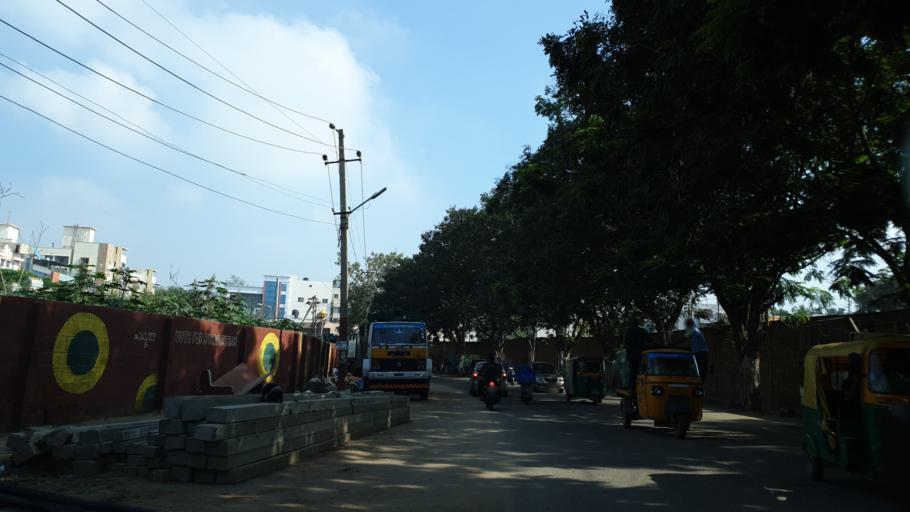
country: IN
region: Karnataka
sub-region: Bangalore Urban
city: Bangalore
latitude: 12.9657
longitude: 77.6829
